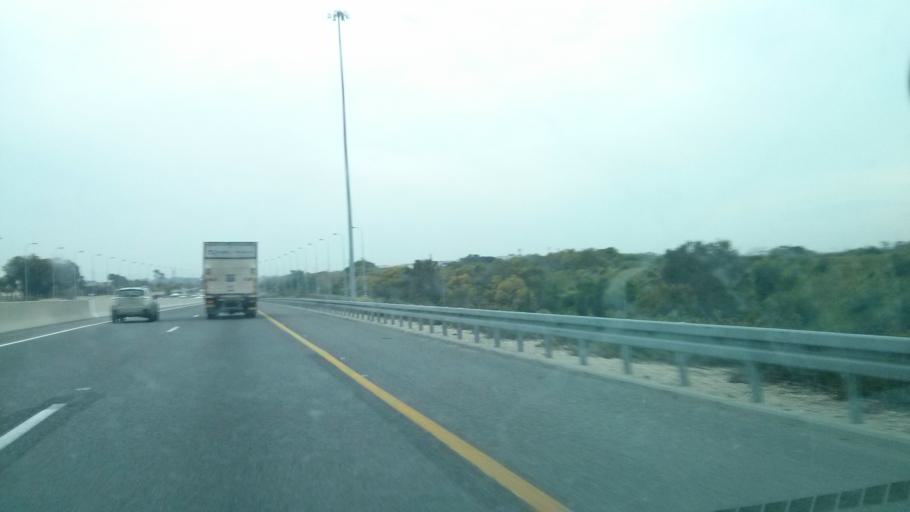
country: IL
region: Haifa
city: Qesarya
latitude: 32.5038
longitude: 34.9146
